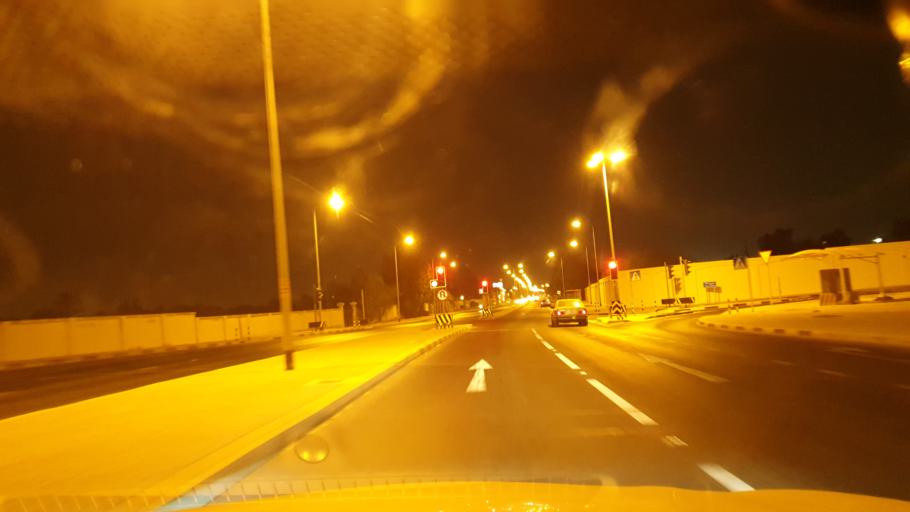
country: BH
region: Manama
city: Jidd Hafs
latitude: 26.2090
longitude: 50.4818
